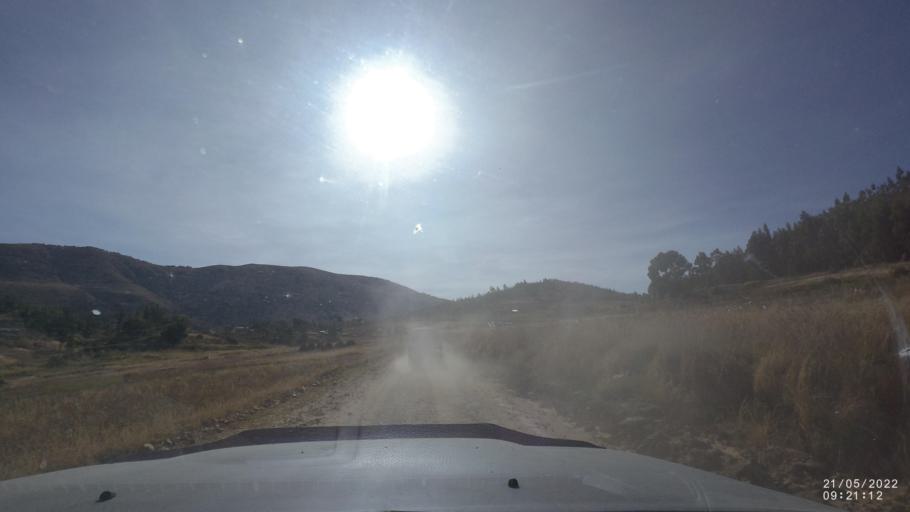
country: BO
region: Cochabamba
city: Cochabamba
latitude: -17.3531
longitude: -66.0177
